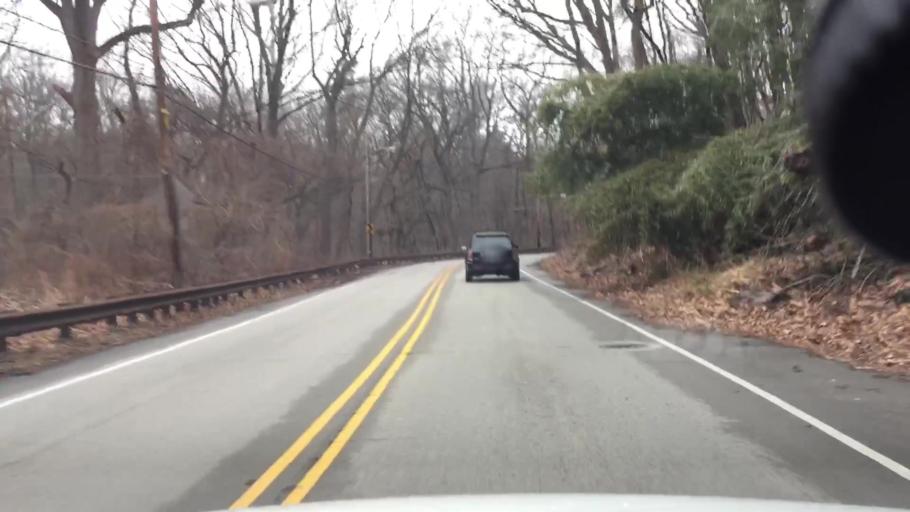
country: US
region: Pennsylvania
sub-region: Montgomery County
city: Wyndmoor
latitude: 40.0589
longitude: -75.2005
